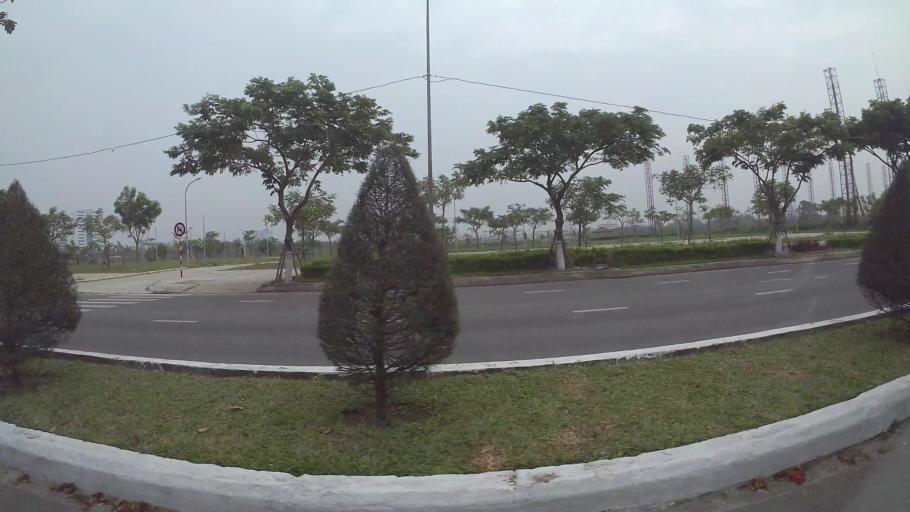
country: VN
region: Da Nang
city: Cam Le
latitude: 16.0264
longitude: 108.2146
